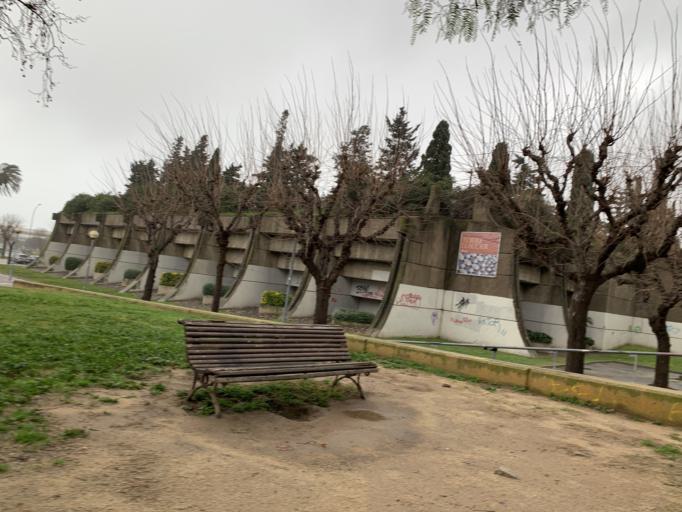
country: ES
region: Catalonia
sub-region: Provincia de Barcelona
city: Mataro
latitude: 41.5317
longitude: 2.4349
